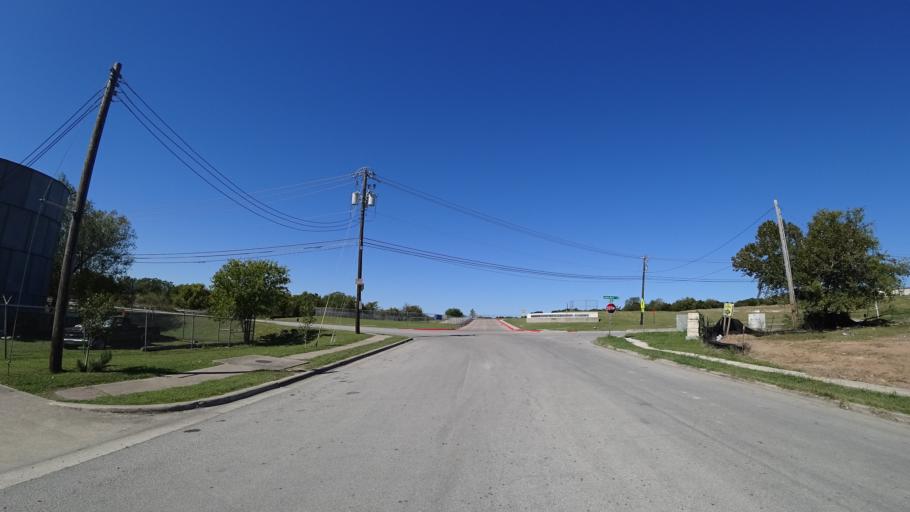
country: US
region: Texas
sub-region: Travis County
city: Hornsby Bend
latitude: 30.3077
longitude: -97.6429
